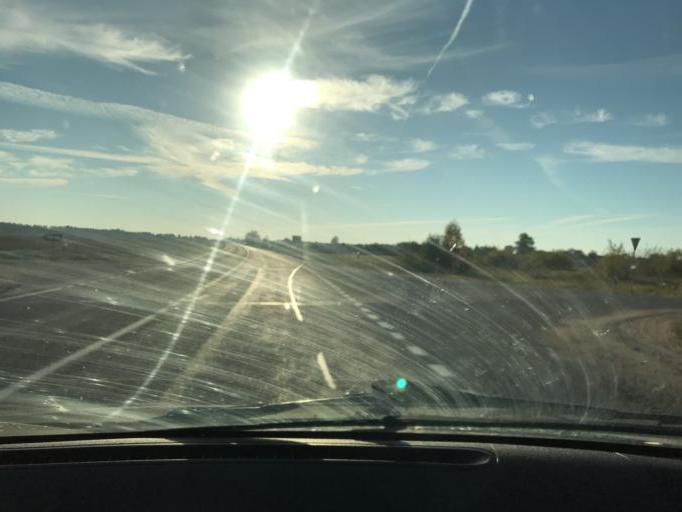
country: BY
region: Brest
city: Horad Kobryn
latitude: 52.2147
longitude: 24.4897
